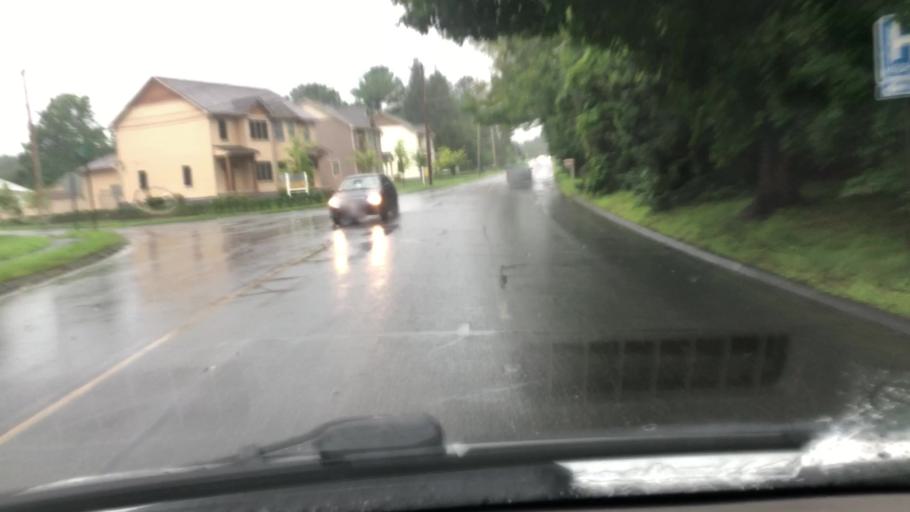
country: US
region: Massachusetts
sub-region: Hampshire County
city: Northampton
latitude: 42.3383
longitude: -72.6492
